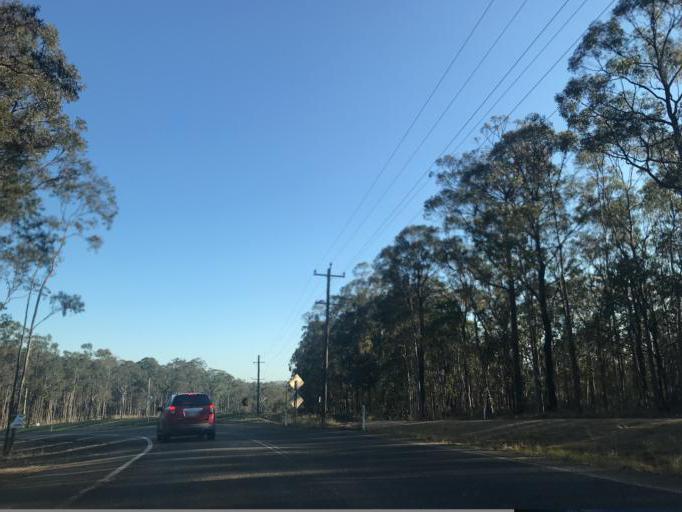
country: AU
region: New South Wales
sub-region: Cessnock
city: Cessnock
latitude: -32.8767
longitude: 151.3111
